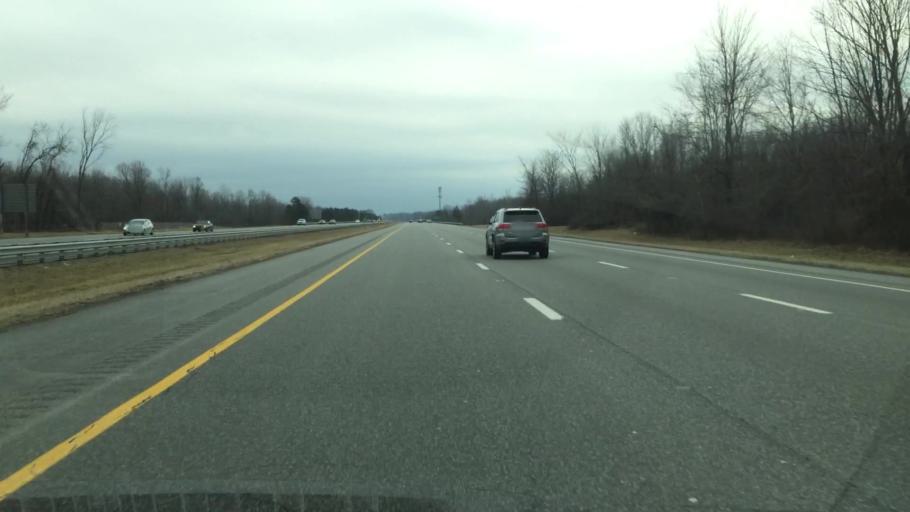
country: US
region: Ohio
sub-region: Cuyahoga County
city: Strongsville
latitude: 41.3004
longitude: -81.8085
